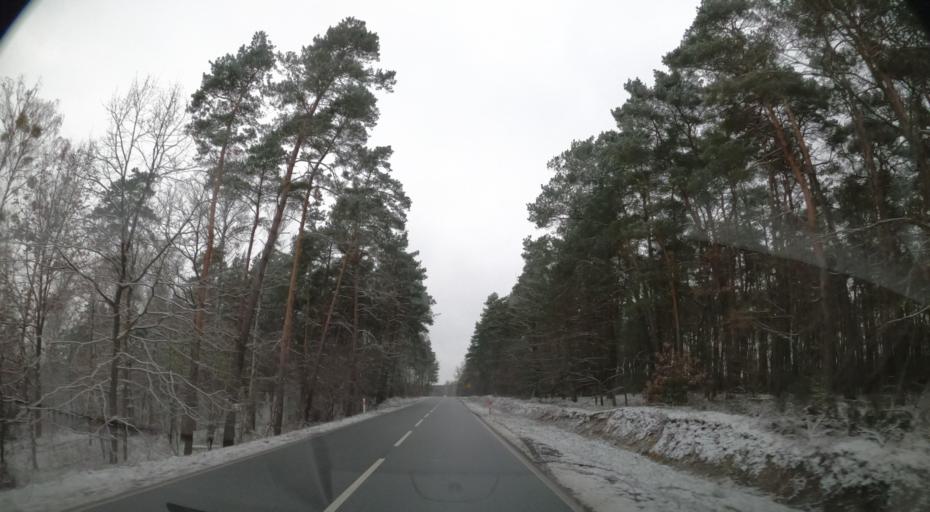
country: PL
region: Kujawsko-Pomorskie
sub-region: Powiat lipnowski
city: Wielgie
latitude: 52.7601
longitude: 19.2321
